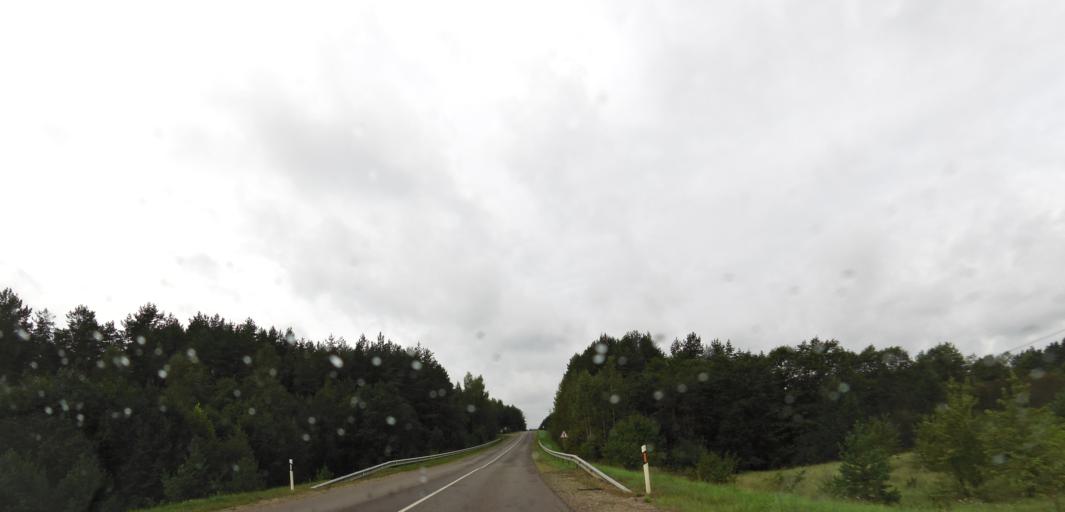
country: LT
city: Moletai
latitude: 55.2141
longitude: 25.3636
